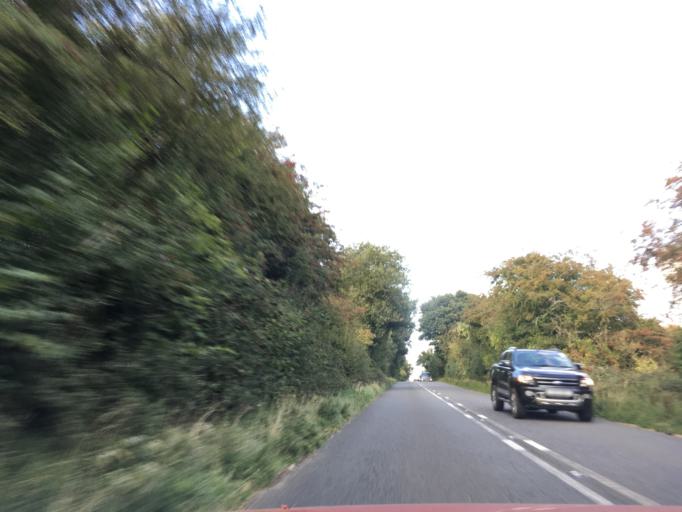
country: GB
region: England
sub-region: Gloucestershire
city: Northleach
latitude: 51.8460
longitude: -1.8247
